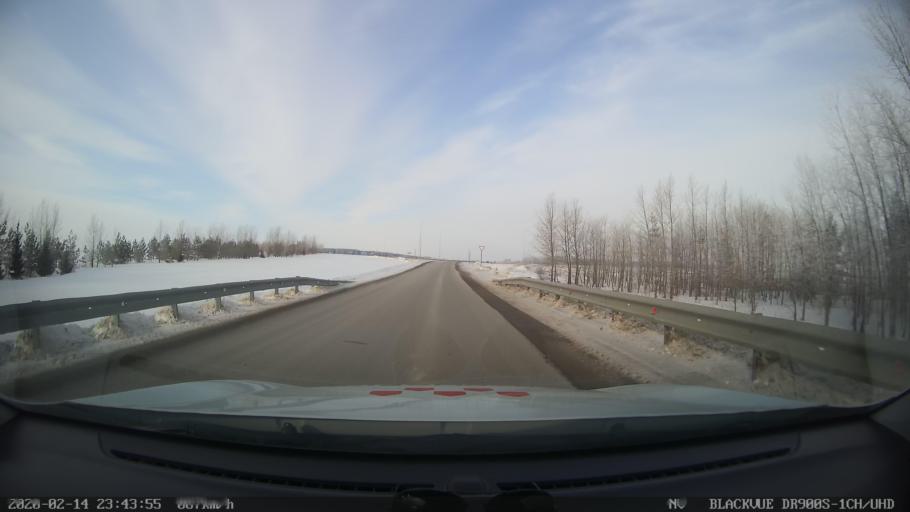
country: RU
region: Tatarstan
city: Kuybyshevskiy Zaton
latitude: 55.2078
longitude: 49.2475
